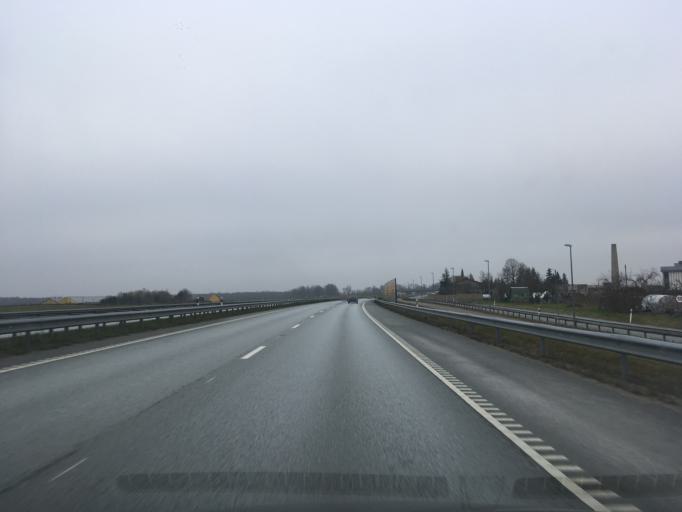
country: EE
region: Ida-Virumaa
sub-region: Johvi vald
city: Johvi
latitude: 59.3806
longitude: 27.3699
